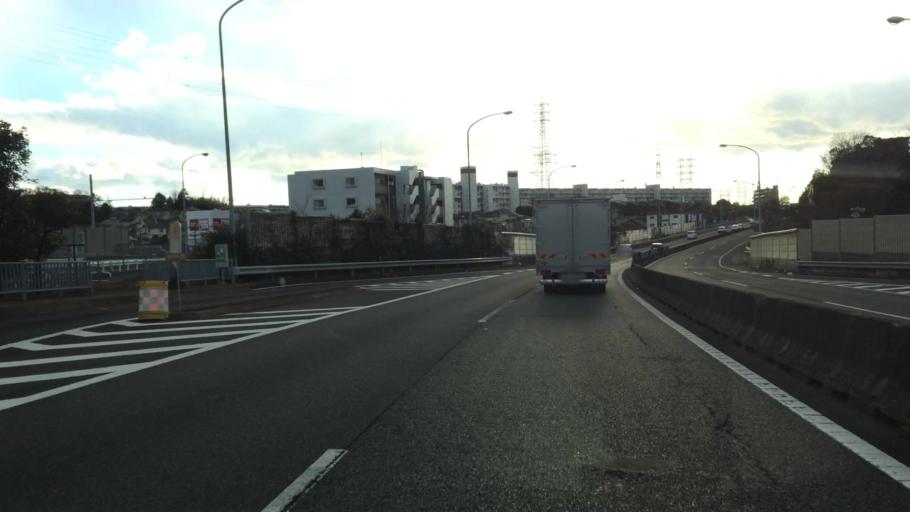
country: JP
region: Kanagawa
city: Yokohama
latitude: 35.4312
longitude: 139.5519
